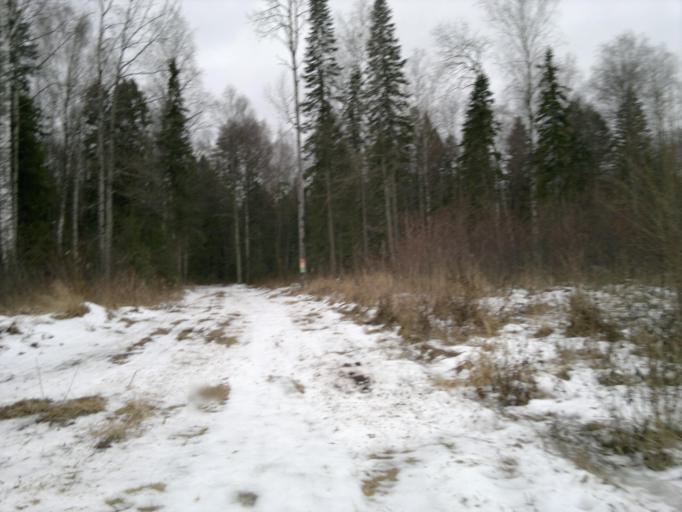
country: RU
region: Mariy-El
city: Yoshkar-Ola
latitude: 56.5952
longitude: 47.9688
